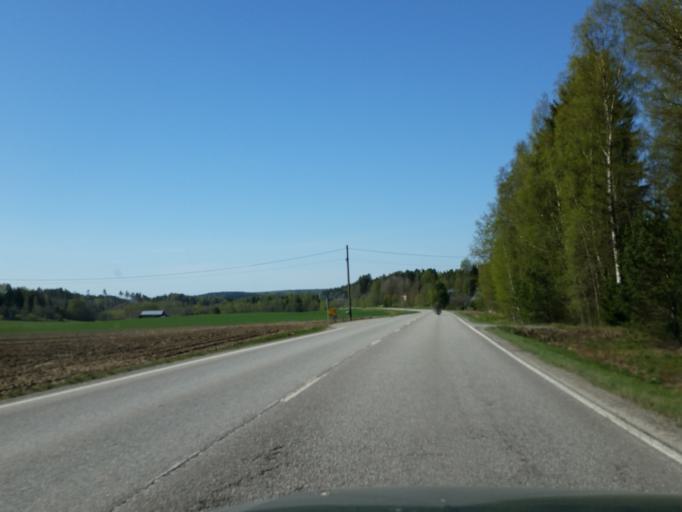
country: FI
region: Uusimaa
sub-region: Helsinki
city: Siuntio
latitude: 60.1855
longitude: 24.2417
